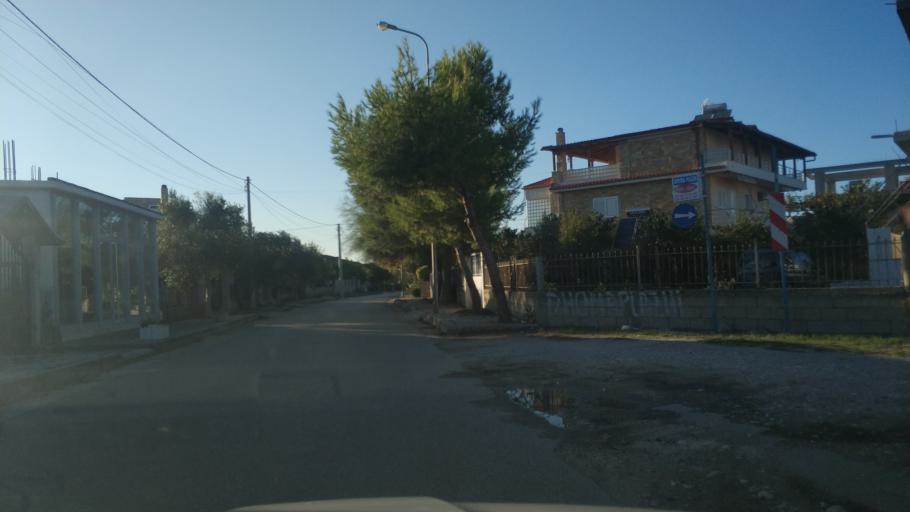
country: AL
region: Vlore
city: Vlore
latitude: 40.5064
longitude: 19.4134
